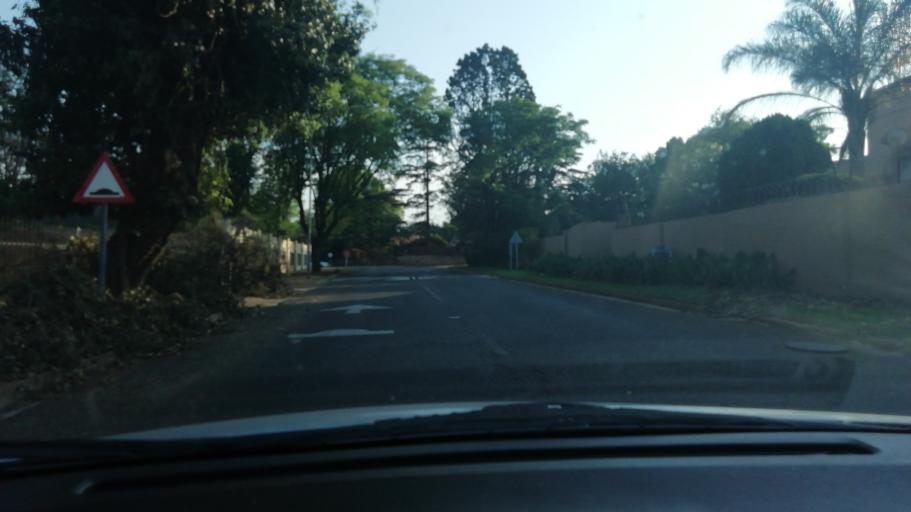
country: ZA
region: Gauteng
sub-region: Ekurhuleni Metropolitan Municipality
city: Benoni
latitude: -26.1901
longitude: 28.2886
